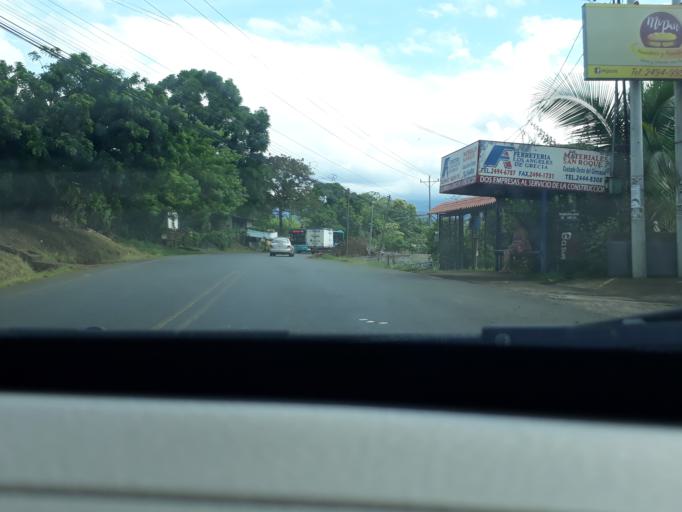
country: CR
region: Alajuela
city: Naranjo
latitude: 10.0415
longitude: -84.3472
